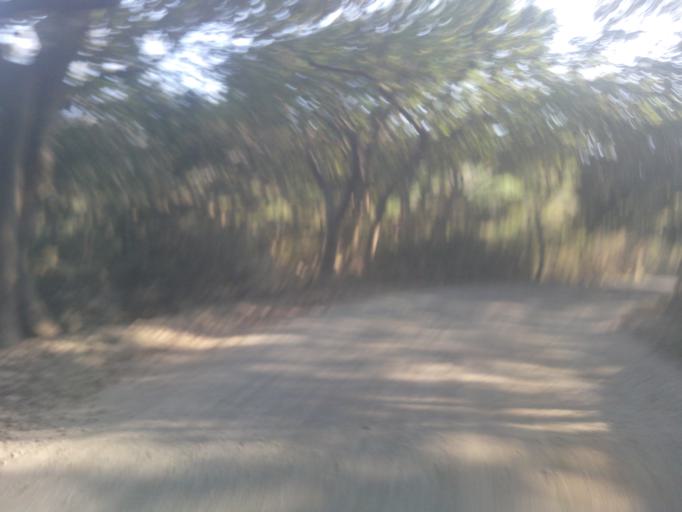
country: CR
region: Guanacaste
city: Samara
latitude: 9.9608
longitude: -85.6657
